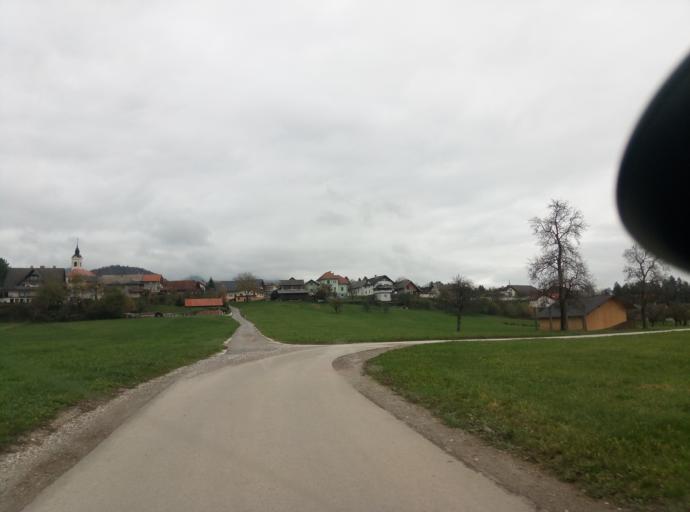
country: SI
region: Preddvor
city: Preddvor
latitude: 46.2769
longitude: 14.4348
